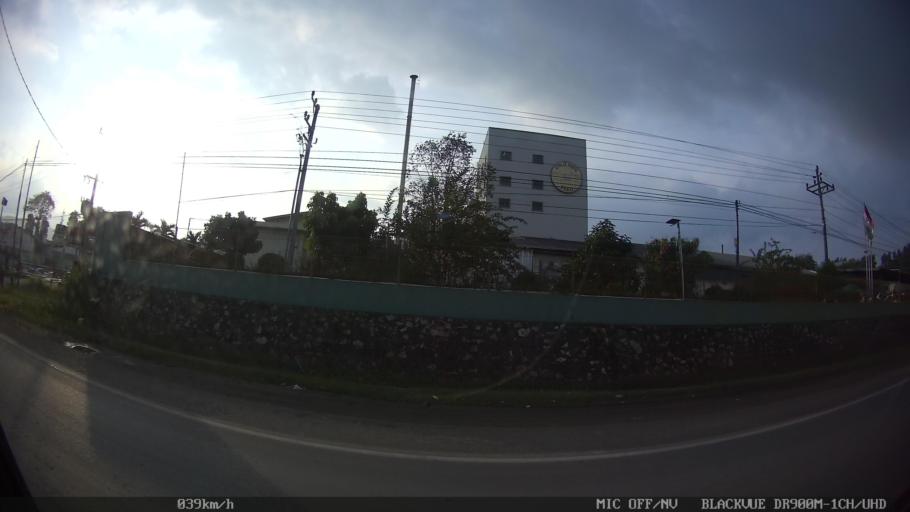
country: ID
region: Lampung
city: Panjang
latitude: -5.4168
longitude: 105.3437
